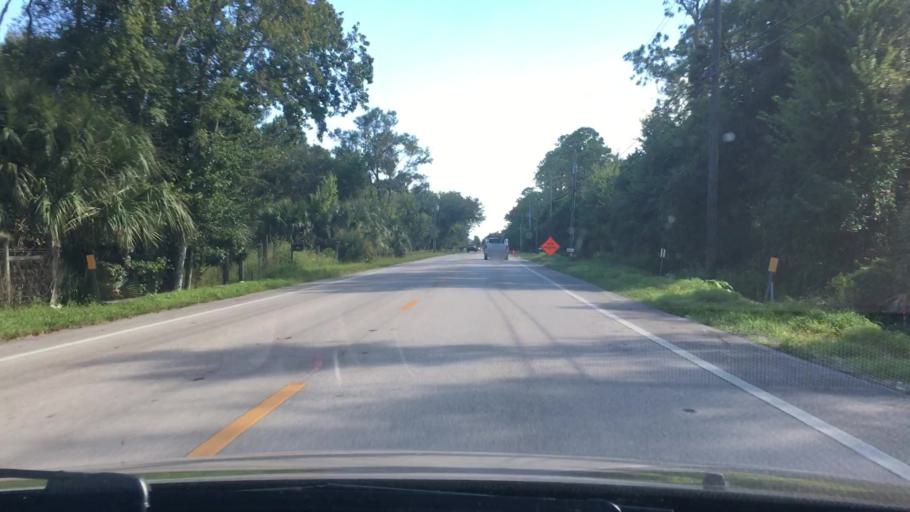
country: US
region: Florida
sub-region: Volusia County
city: Samsula-Spruce Creek
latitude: 29.0961
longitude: -81.0687
